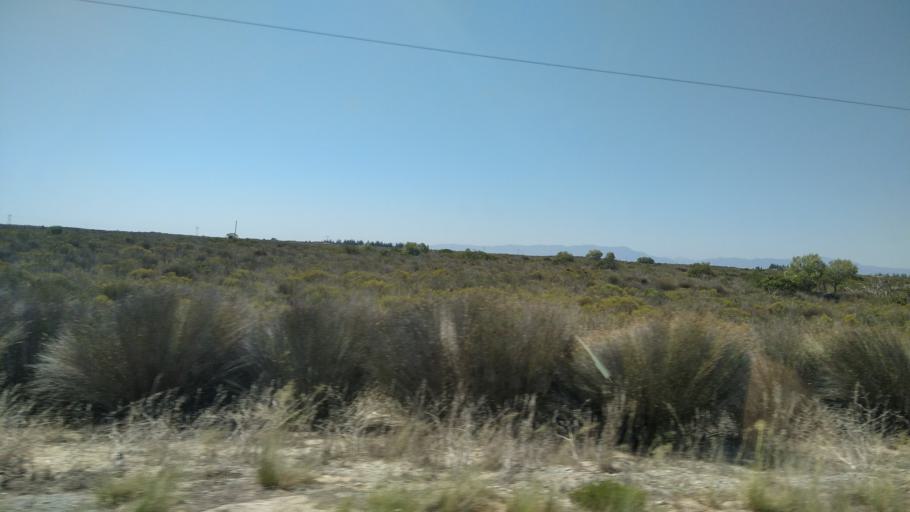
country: ZA
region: Western Cape
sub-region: West Coast District Municipality
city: Vredenburg
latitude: -33.0164
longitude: 18.2520
